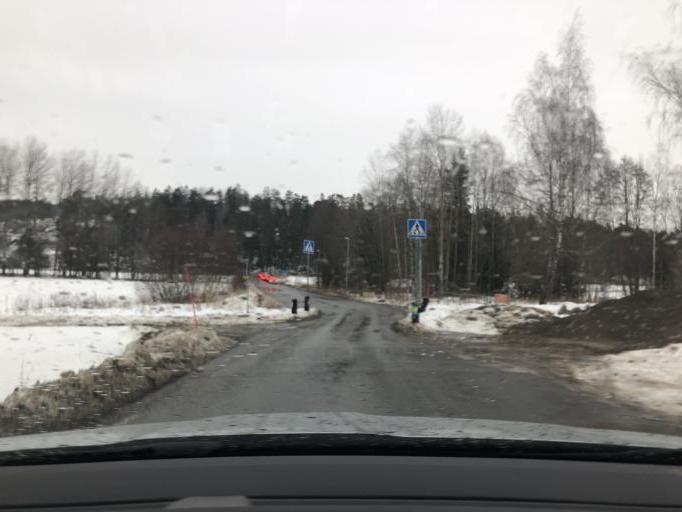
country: SE
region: Stockholm
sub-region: Botkyrka Kommun
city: Tullinge
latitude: 59.2376
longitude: 17.9023
